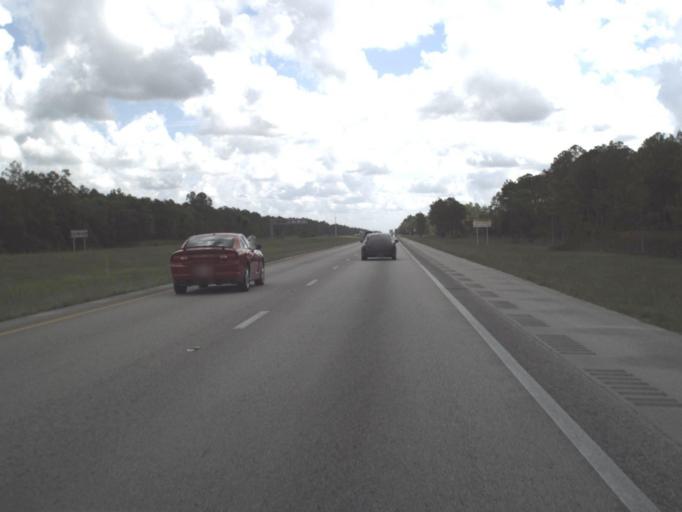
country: US
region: Florida
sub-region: Collier County
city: Golden Gate
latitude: 26.1548
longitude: -81.6512
